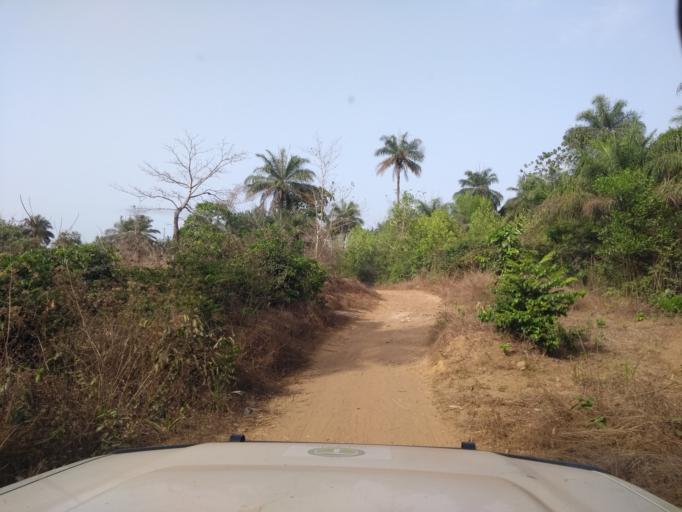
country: GN
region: Kindia
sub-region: Prefecture de Dubreka
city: Dubreka
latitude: 9.8163
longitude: -13.5584
